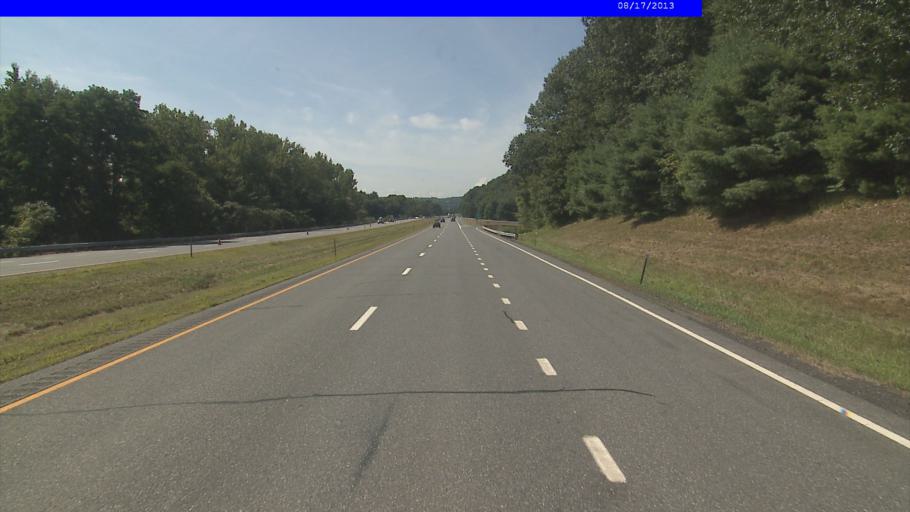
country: US
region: Vermont
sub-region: Windham County
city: Brattleboro
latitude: 42.8894
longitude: -72.5564
